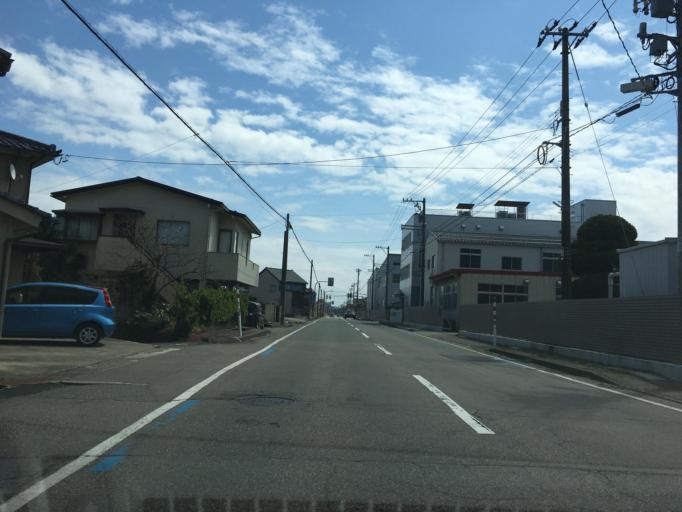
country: JP
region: Toyama
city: Nishishinminato
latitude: 36.8040
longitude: 137.0509
